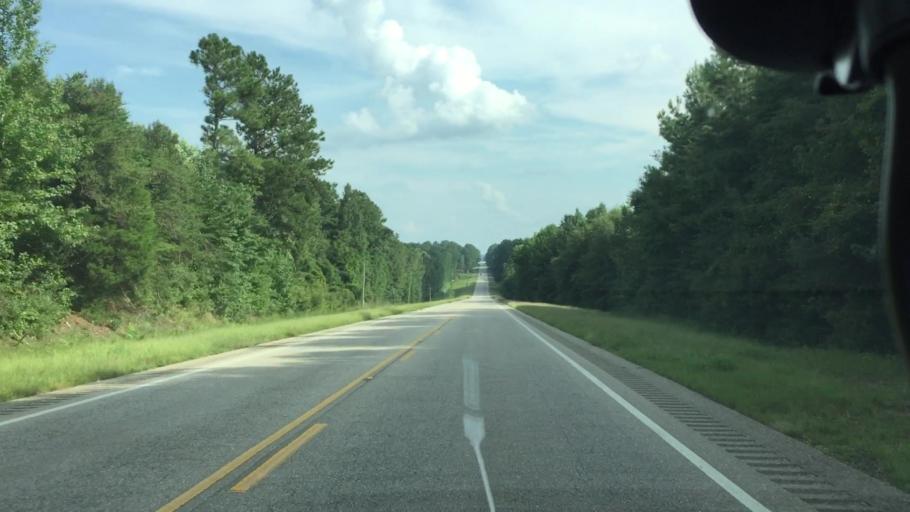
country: US
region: Alabama
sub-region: Pike County
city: Troy
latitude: 31.6721
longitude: -85.9557
